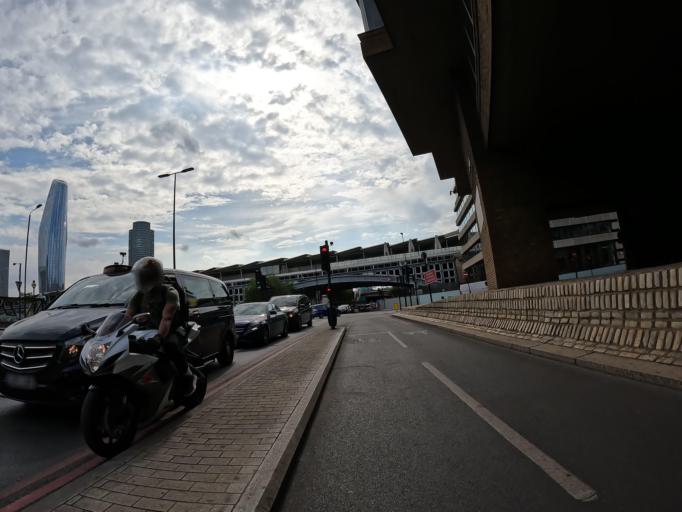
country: GB
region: England
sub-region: Greater London
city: Harringay
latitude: 51.5831
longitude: -0.0904
